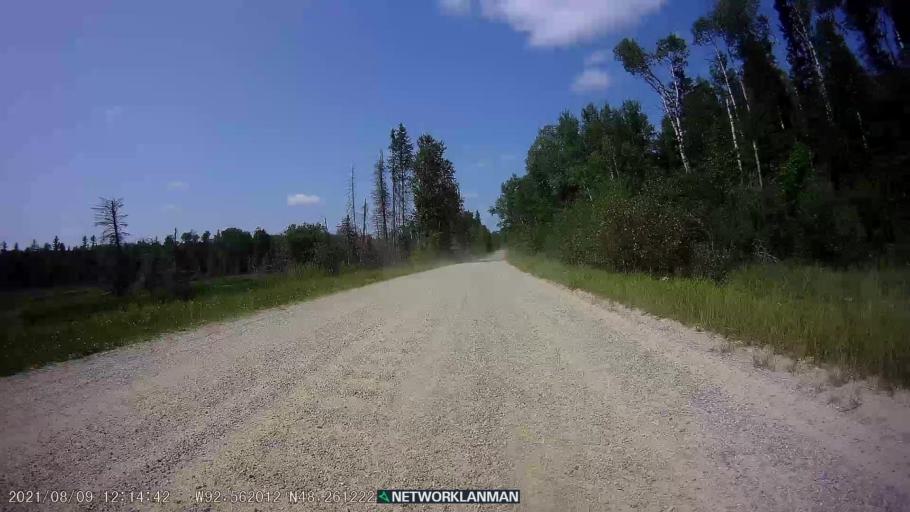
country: US
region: Minnesota
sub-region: Saint Louis County
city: Parkville
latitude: 48.2612
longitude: -92.5619
